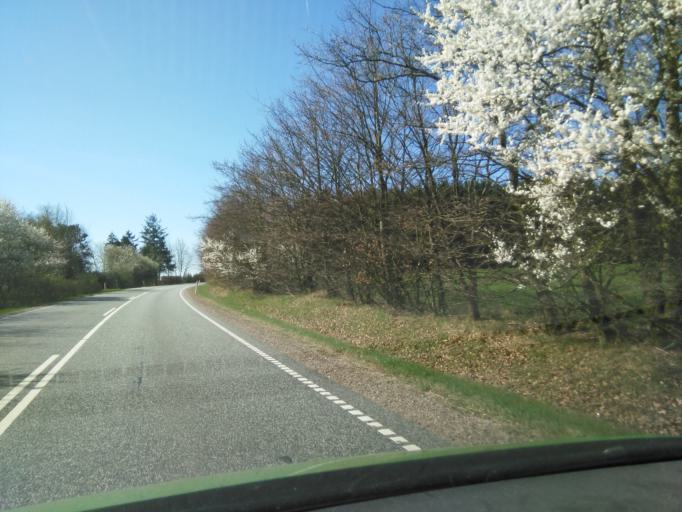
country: DK
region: South Denmark
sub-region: Billund Kommune
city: Billund
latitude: 55.7600
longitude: 9.1428
